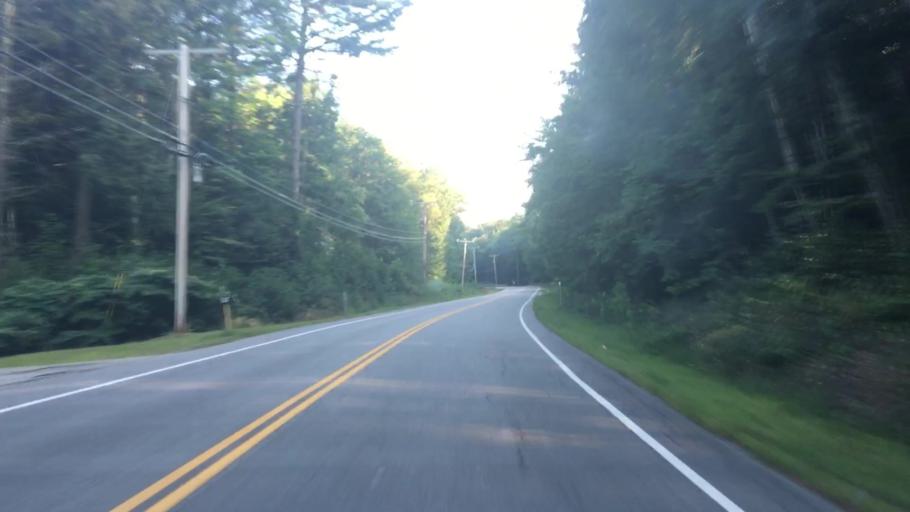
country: US
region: New Hampshire
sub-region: Belknap County
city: Laconia
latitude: 43.4996
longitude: -71.4466
